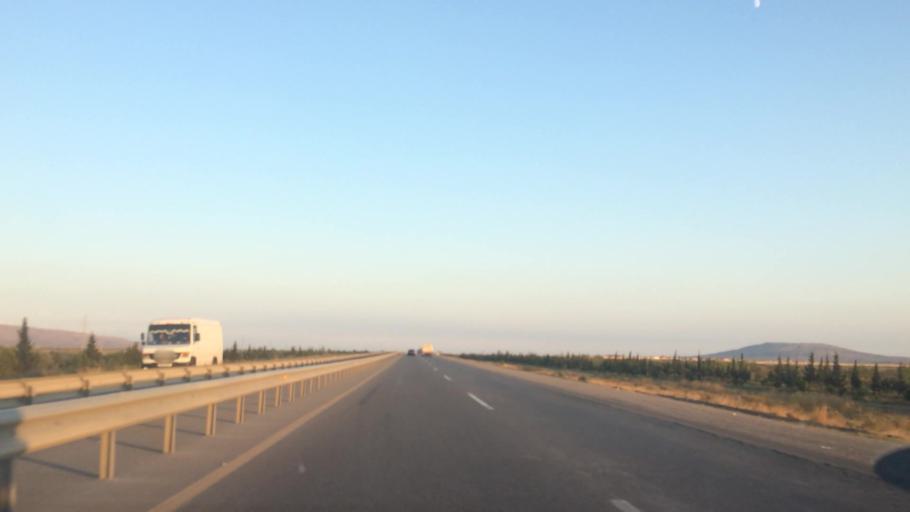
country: AZ
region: Baki
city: Qobustan
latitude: 39.9915
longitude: 49.1952
